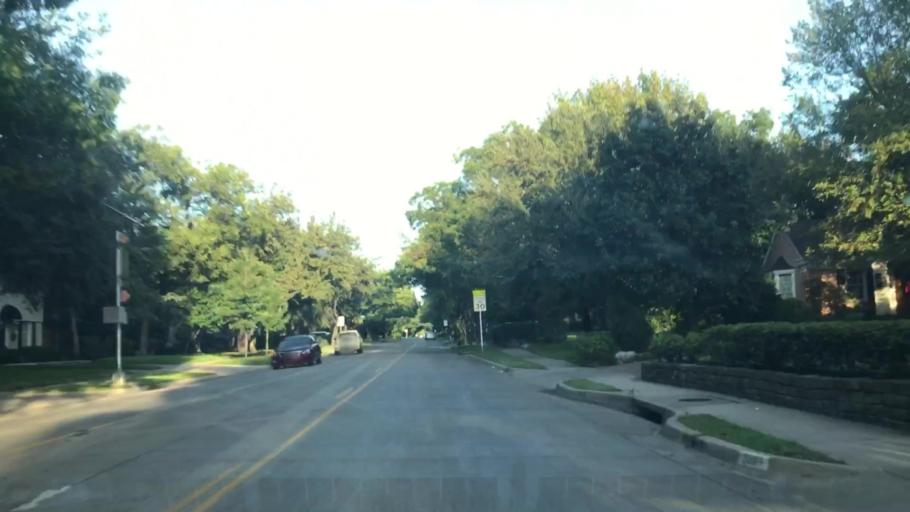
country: US
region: Texas
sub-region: Dallas County
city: University Park
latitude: 32.8511
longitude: -96.7862
